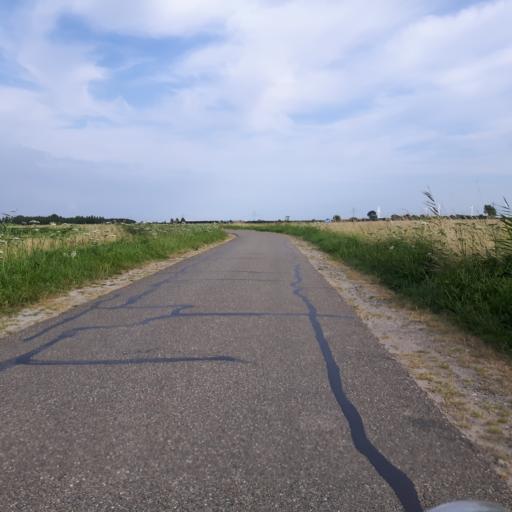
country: NL
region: Zeeland
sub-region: Gemeente Goes
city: Goes
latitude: 51.4812
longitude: 3.9210
